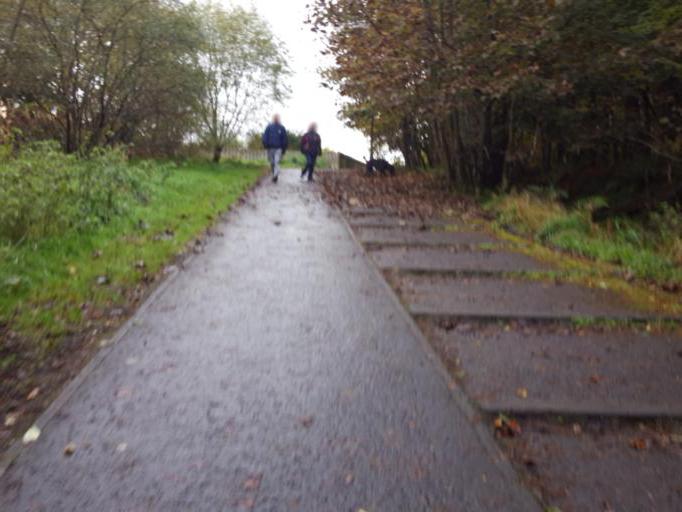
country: GB
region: Scotland
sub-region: West Lothian
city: Livingston
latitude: 55.8891
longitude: -3.5440
